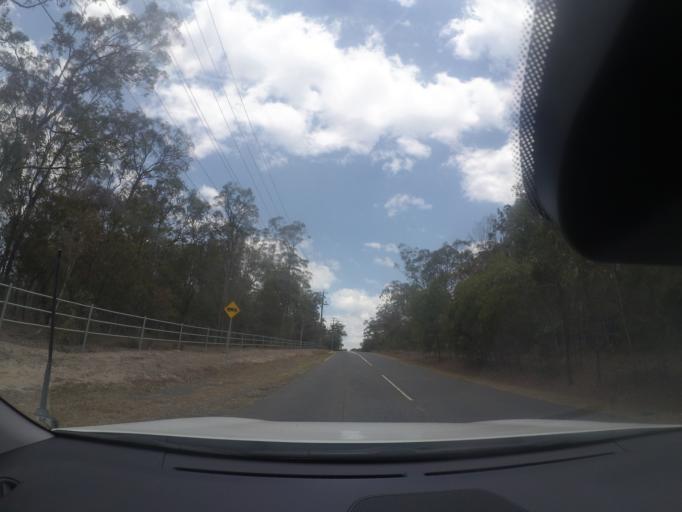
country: AU
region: Queensland
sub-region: Logan
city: Woodridge
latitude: -27.6222
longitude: 153.0939
